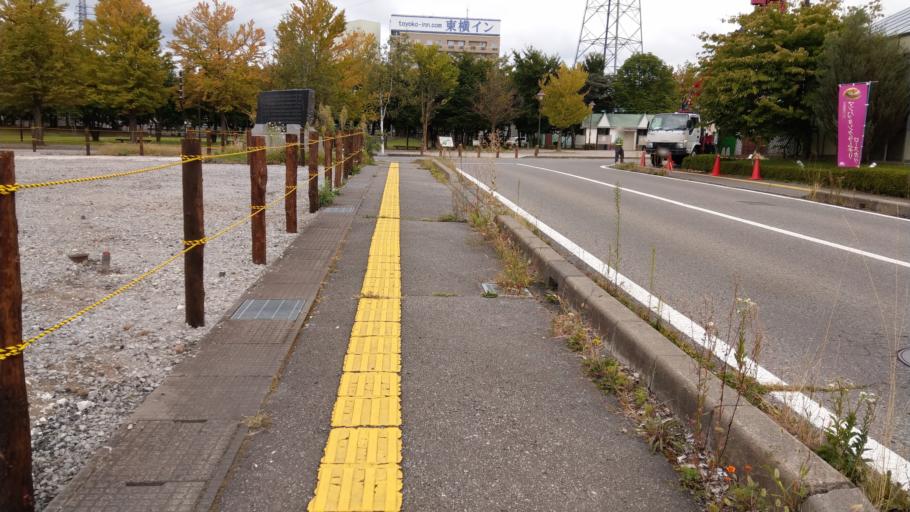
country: JP
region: Nagano
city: Komoro
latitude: 36.2765
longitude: 138.4640
